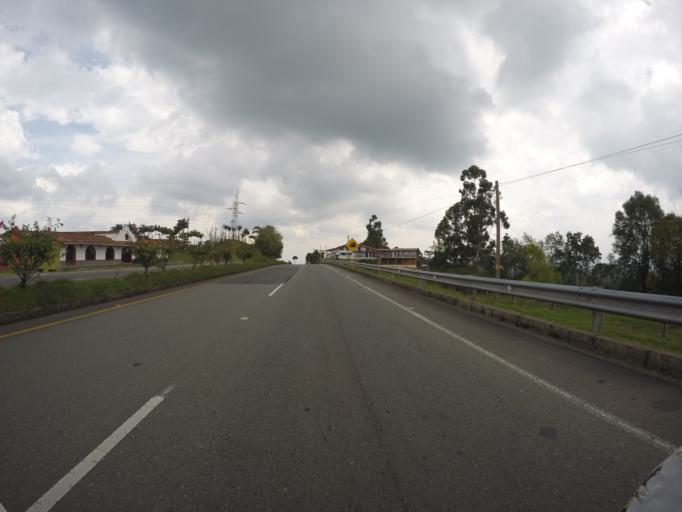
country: CO
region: Quindio
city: Filandia
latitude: 4.7242
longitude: -75.6278
